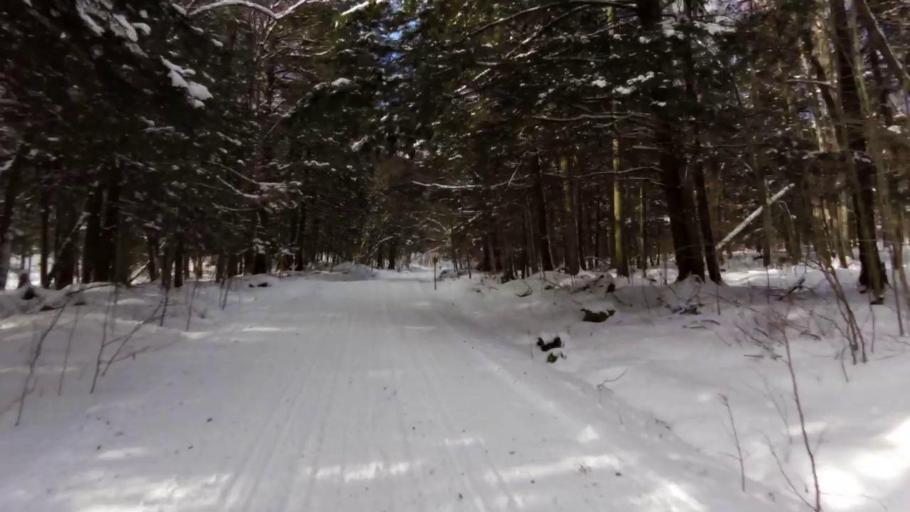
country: US
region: Pennsylvania
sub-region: McKean County
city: Bradford
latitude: 42.0272
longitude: -78.7007
